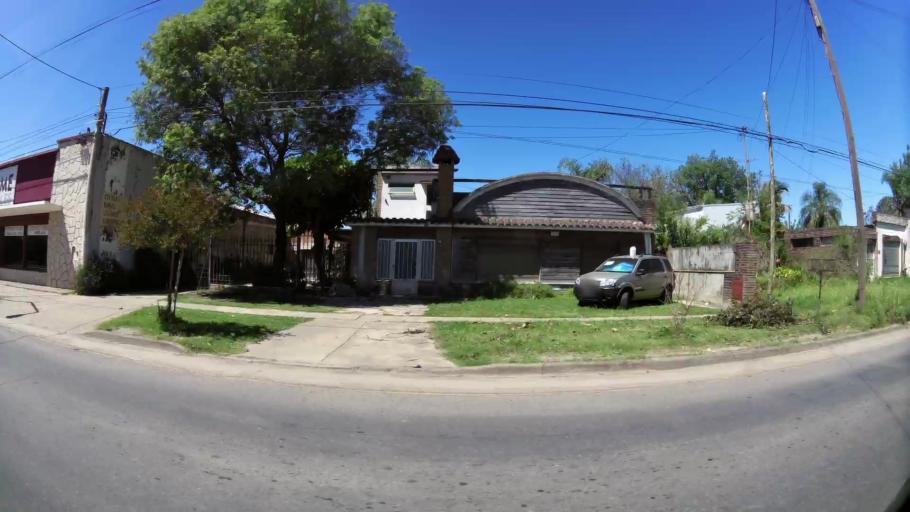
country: AR
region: Santa Fe
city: Esperanza
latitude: -31.4450
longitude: -60.9196
